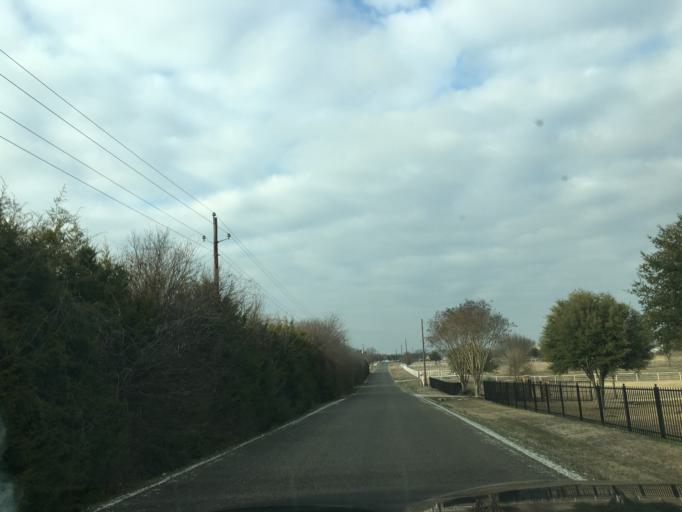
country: US
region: Texas
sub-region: Ellis County
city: Red Oak
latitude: 32.4809
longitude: -96.7893
